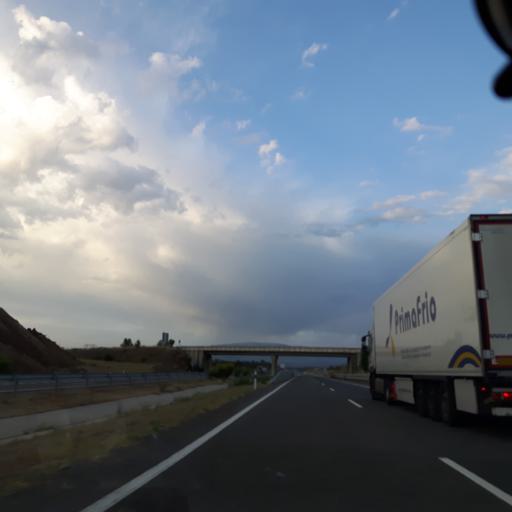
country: ES
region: Castille and Leon
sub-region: Provincia de Salamanca
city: Fuentes de Bejar
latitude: 40.5245
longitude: -5.6716
